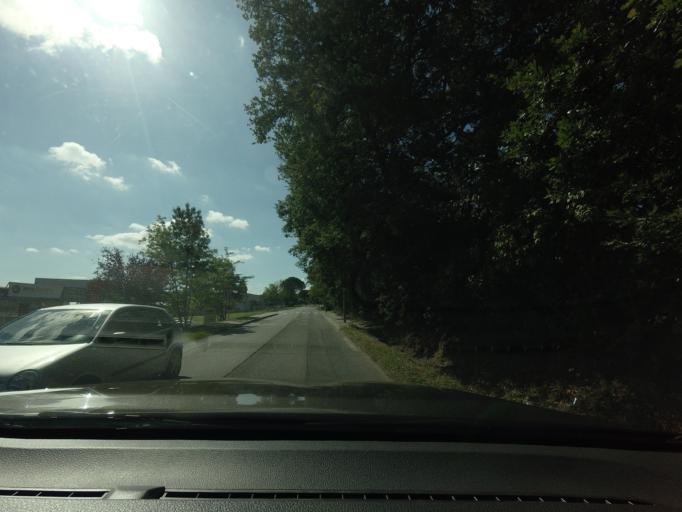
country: FR
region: Midi-Pyrenees
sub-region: Departement de la Haute-Garonne
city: Cornebarrieu
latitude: 43.6481
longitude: 1.3354
